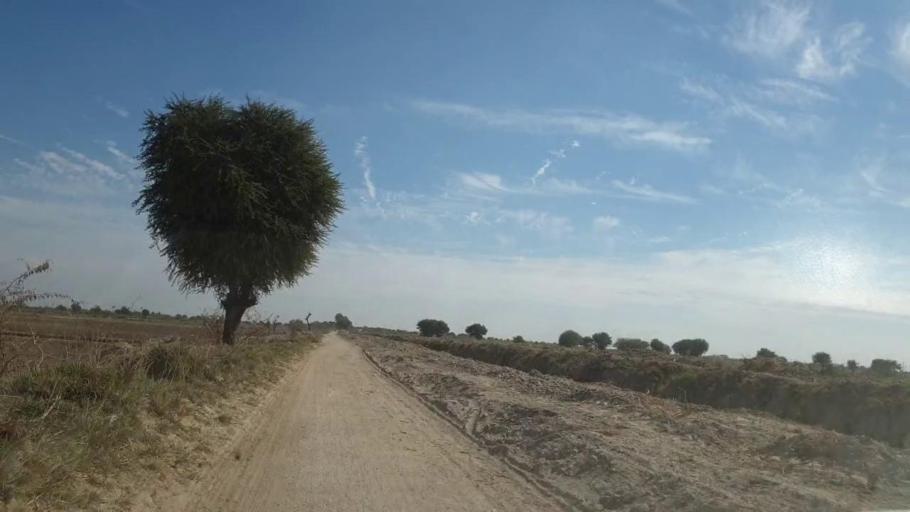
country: PK
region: Sindh
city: Pithoro
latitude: 25.5448
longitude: 69.2988
